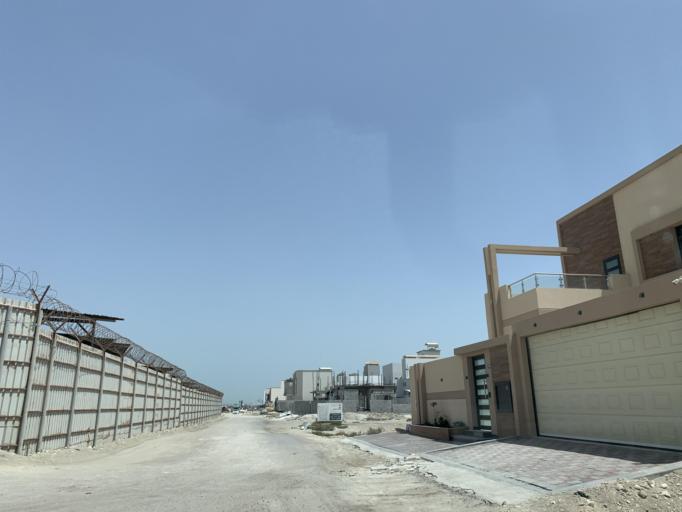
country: BH
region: Northern
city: Sitrah
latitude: 26.1478
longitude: 50.5994
